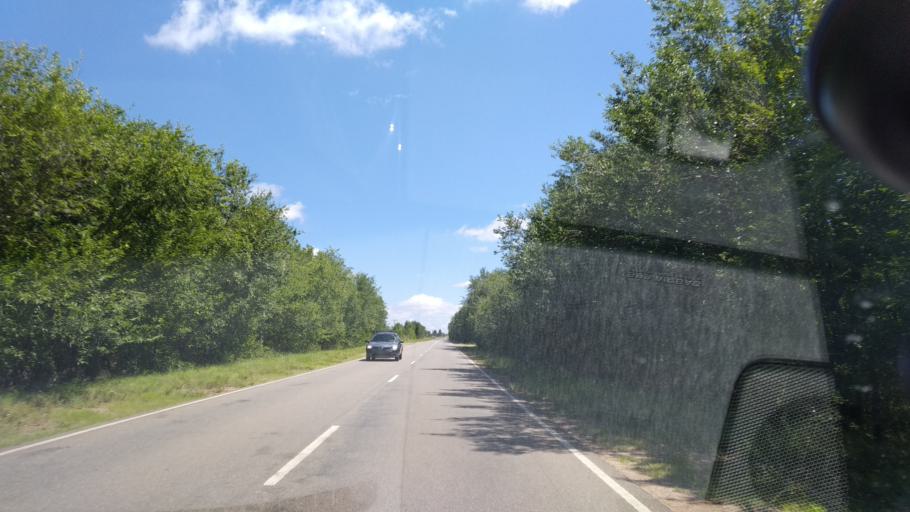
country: AR
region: Cordoba
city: Villa Cura Brochero
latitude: -31.5601
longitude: -65.1122
